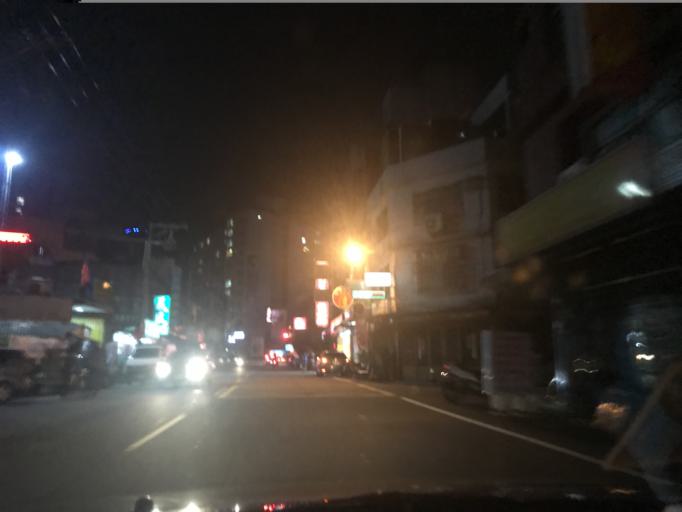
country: TW
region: Taiwan
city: Taoyuan City
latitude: 24.9511
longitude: 121.2118
